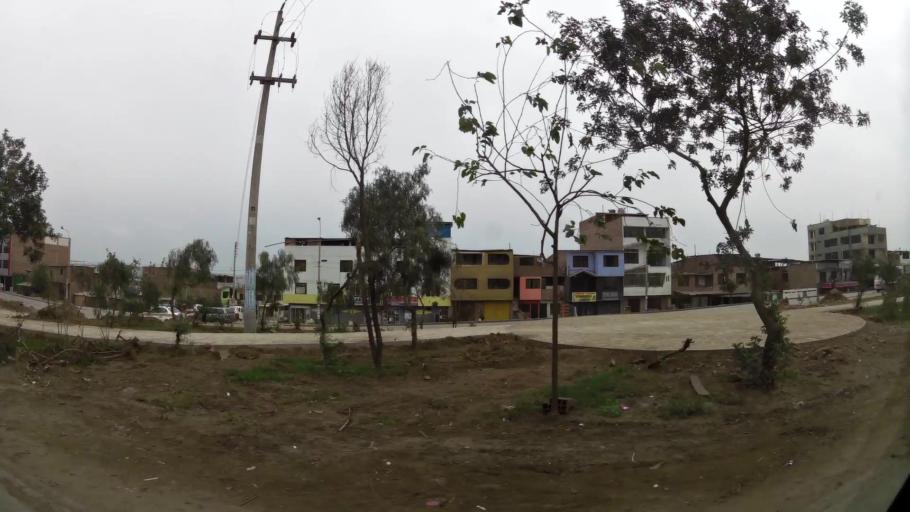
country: PE
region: Lima
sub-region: Lima
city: Surco
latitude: -12.2155
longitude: -76.9471
